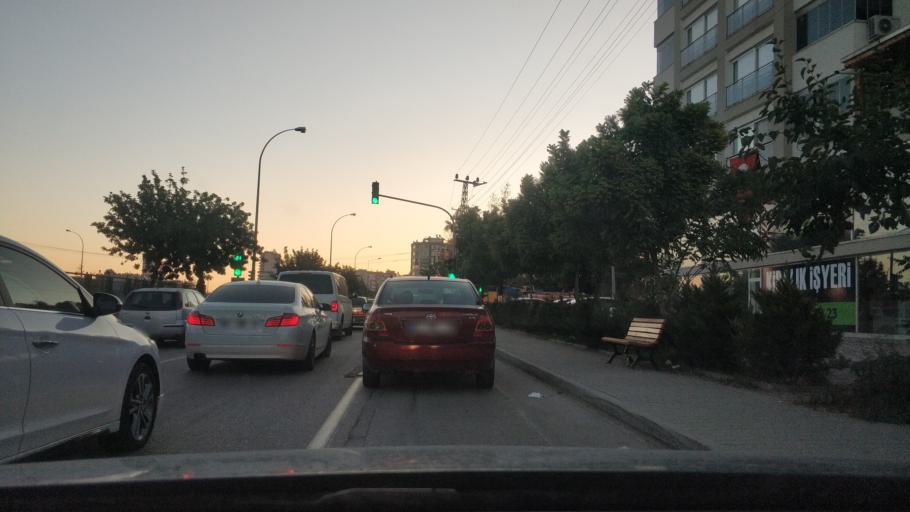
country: TR
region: Adana
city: Seyhan
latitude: 37.0107
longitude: 35.2967
